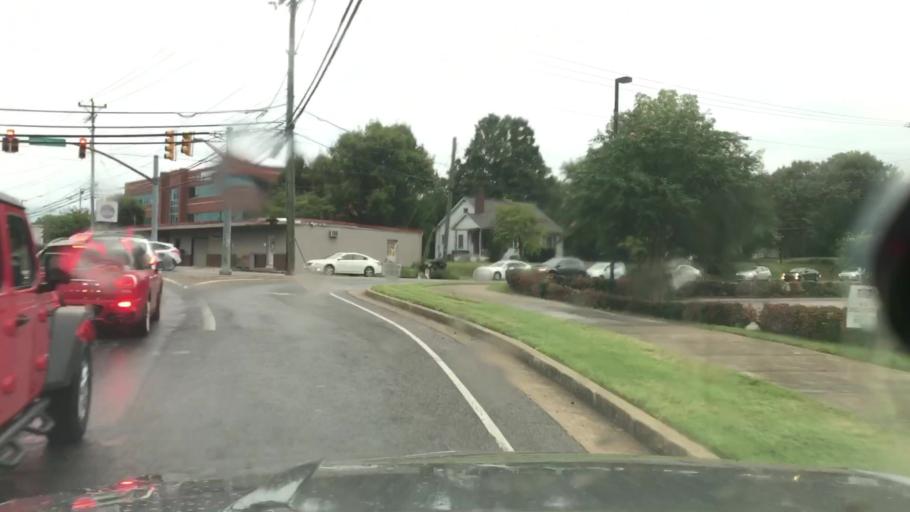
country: US
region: Tennessee
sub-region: Davidson County
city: Lakewood
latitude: 36.1748
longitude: -86.6147
